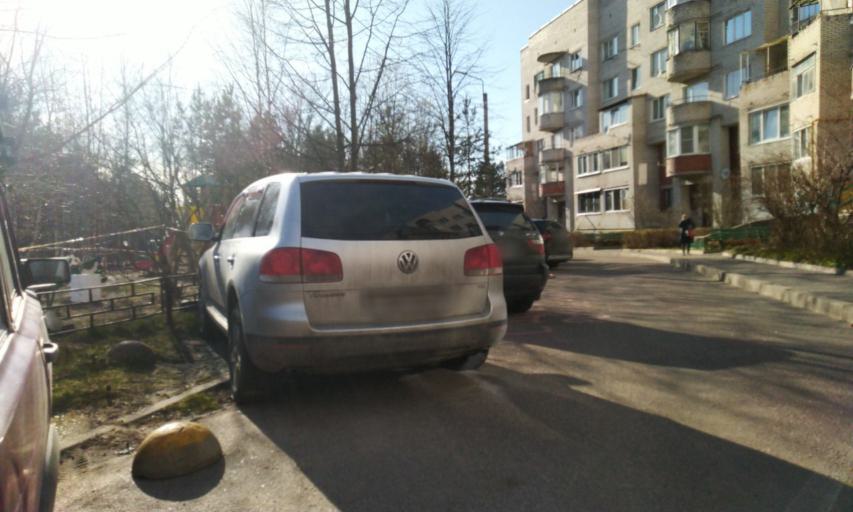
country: RU
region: Leningrad
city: Toksovo
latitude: 60.1212
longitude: 30.4997
